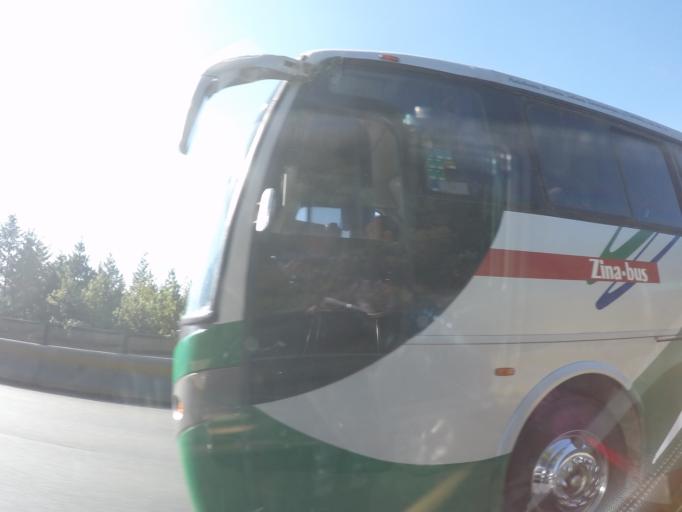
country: MX
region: Mexico City
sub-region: Cuajimalpa de Morelos
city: San Lorenzo Acopilco
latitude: 19.3266
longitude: -99.3173
